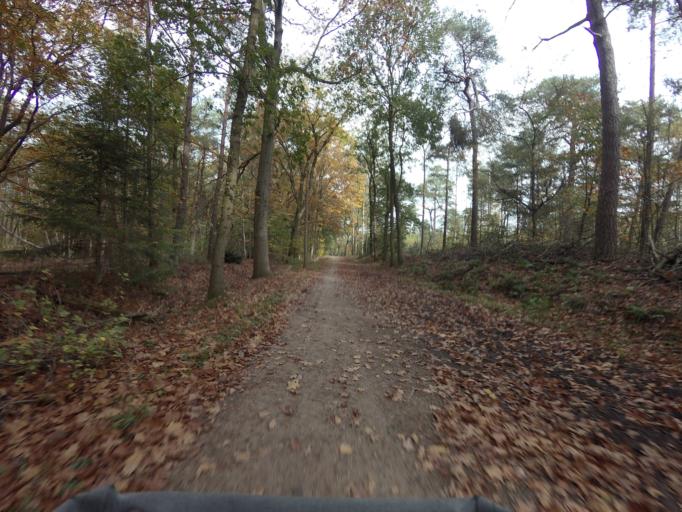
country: NL
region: North Holland
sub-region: Gemeente Hilversum
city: Hilversum
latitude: 52.1904
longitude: 5.2035
